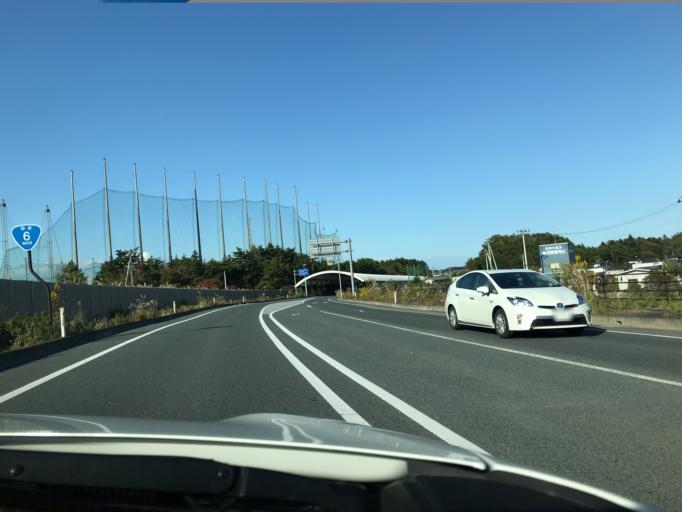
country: JP
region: Miyagi
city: Marumori
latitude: 37.7783
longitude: 140.9397
